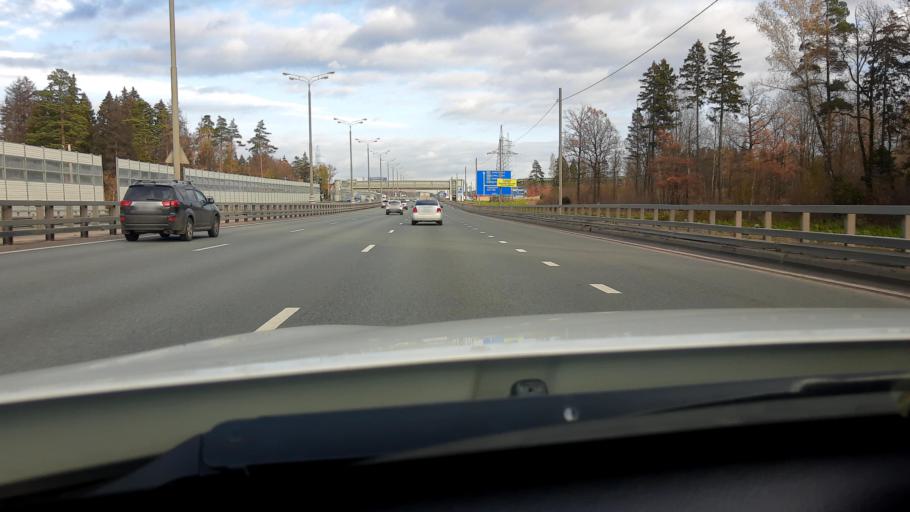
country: RU
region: Moskovskaya
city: Selyatino
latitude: 55.5201
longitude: 37.0033
